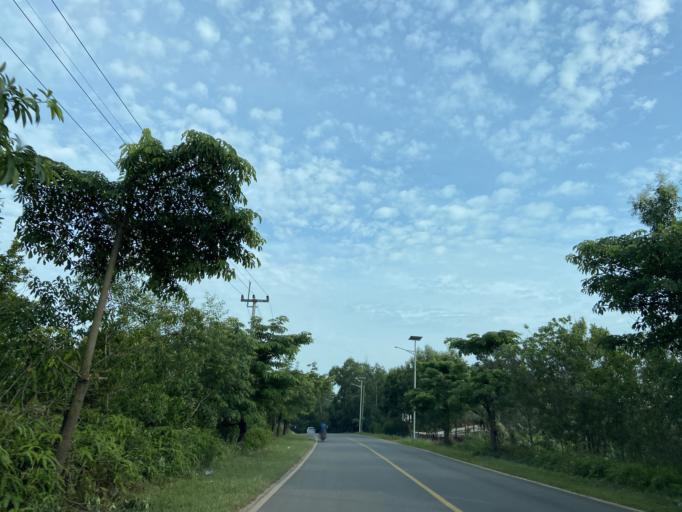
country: ID
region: Riau Islands
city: Tanjungpinang
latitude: 0.9333
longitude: 104.1092
